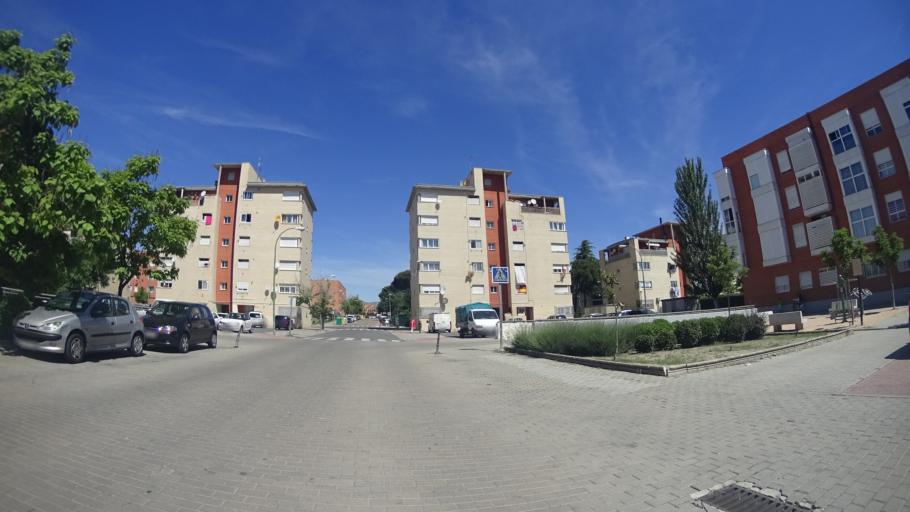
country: ES
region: Madrid
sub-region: Provincia de Madrid
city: Collado-Villalba
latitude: 40.6377
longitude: -4.0104
